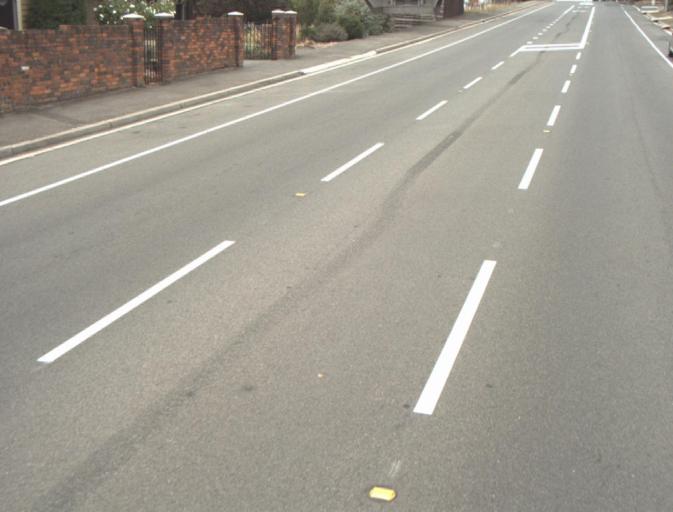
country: AU
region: Tasmania
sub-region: Launceston
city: Newstead
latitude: -41.4563
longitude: 147.1783
